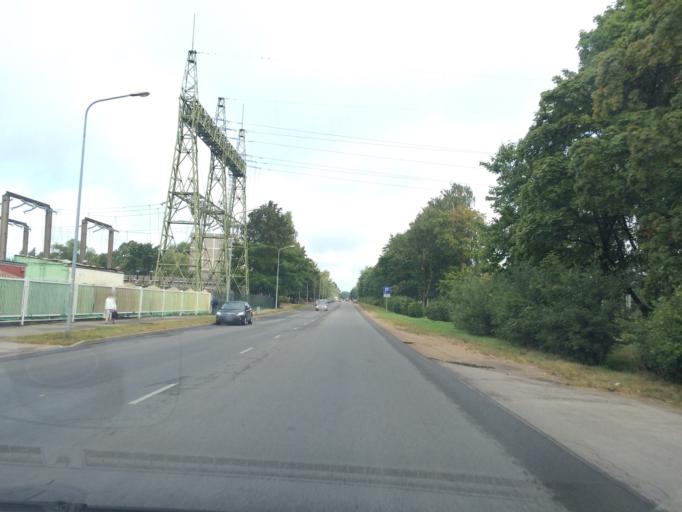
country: LV
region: Kekava
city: Kekava
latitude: 56.9049
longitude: 24.2096
